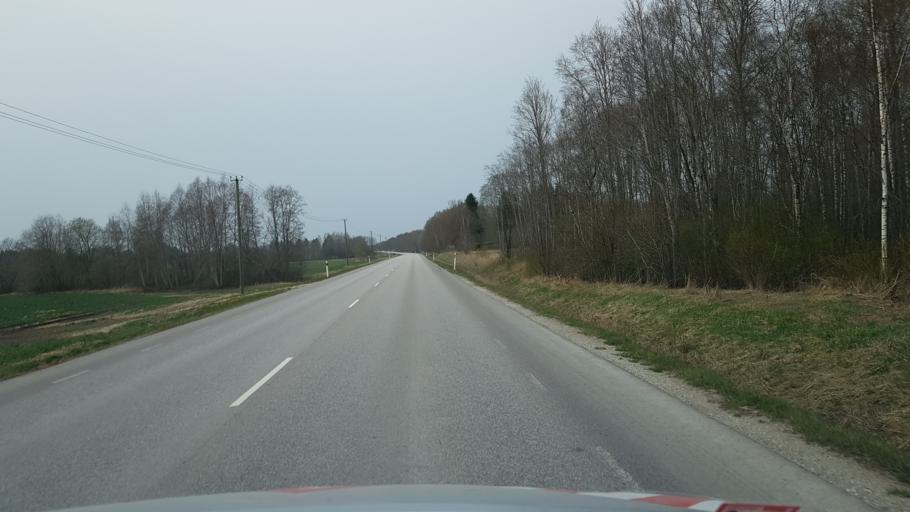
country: EE
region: Harju
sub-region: Joelaehtme vald
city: Loo
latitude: 59.3869
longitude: 24.9928
